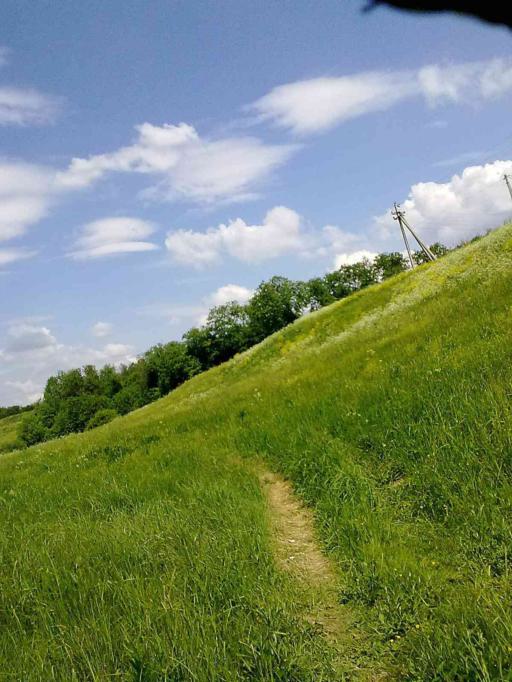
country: RU
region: Moskovskaya
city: Filimonki
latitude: 55.5769
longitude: 37.3444
